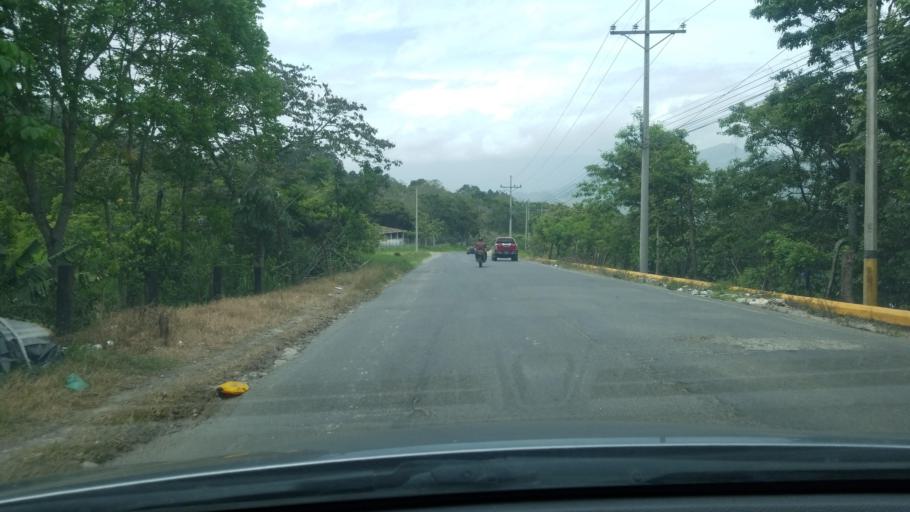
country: HN
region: Copan
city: Santa Rosa de Copan
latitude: 14.7496
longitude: -88.7716
